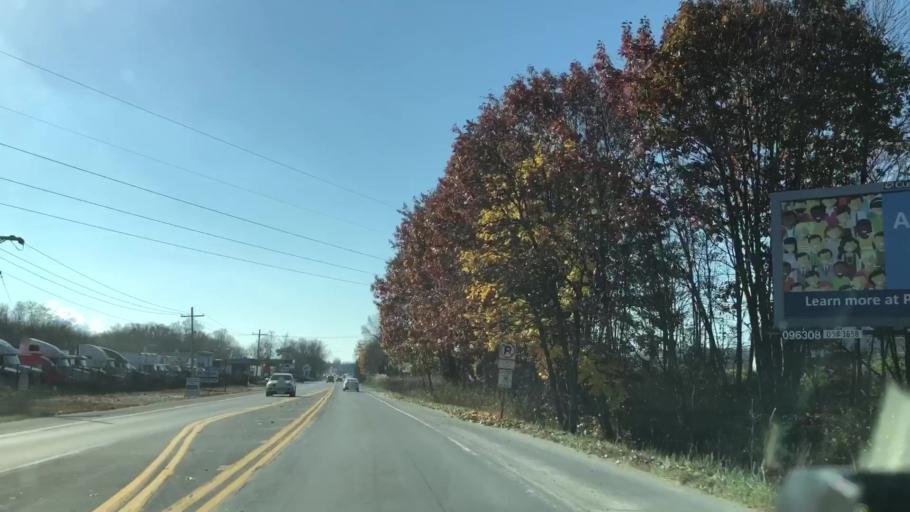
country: US
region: Pennsylvania
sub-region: Berks County
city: New Berlinville
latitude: 40.3587
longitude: -75.6279
